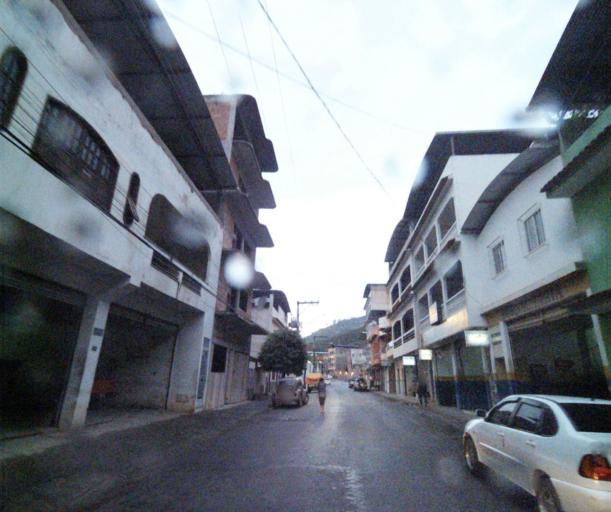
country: BR
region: Espirito Santo
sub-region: Muniz Freire
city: Muniz Freire
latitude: -20.4658
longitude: -41.4142
